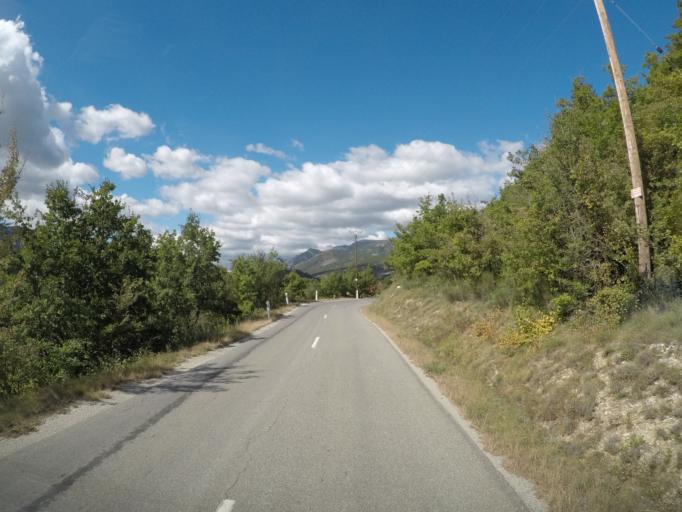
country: FR
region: Provence-Alpes-Cote d'Azur
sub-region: Departement des Hautes-Alpes
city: Laragne-Monteglin
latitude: 44.1664
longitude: 5.7659
